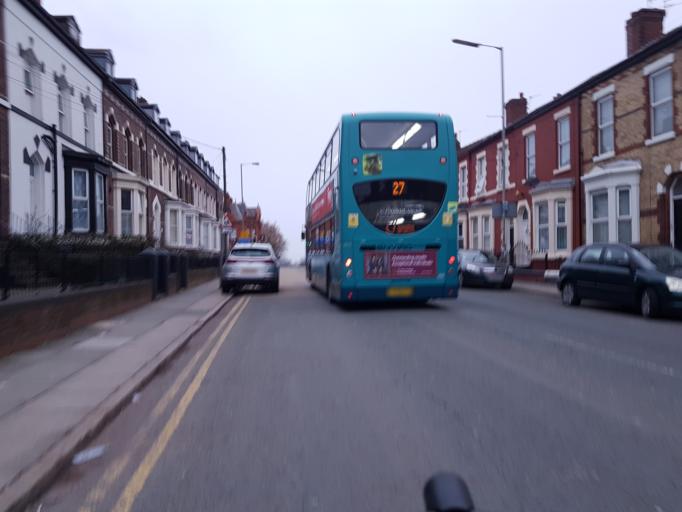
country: GB
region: England
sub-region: Liverpool
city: Liverpool
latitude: 53.4308
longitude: -2.9666
